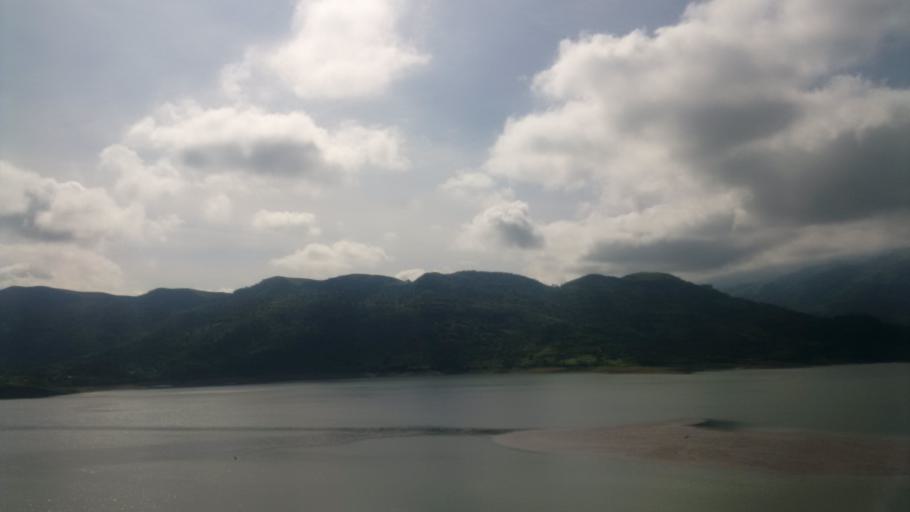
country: HT
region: Centre
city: Mirebalais
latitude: 18.9099
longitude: -72.0193
